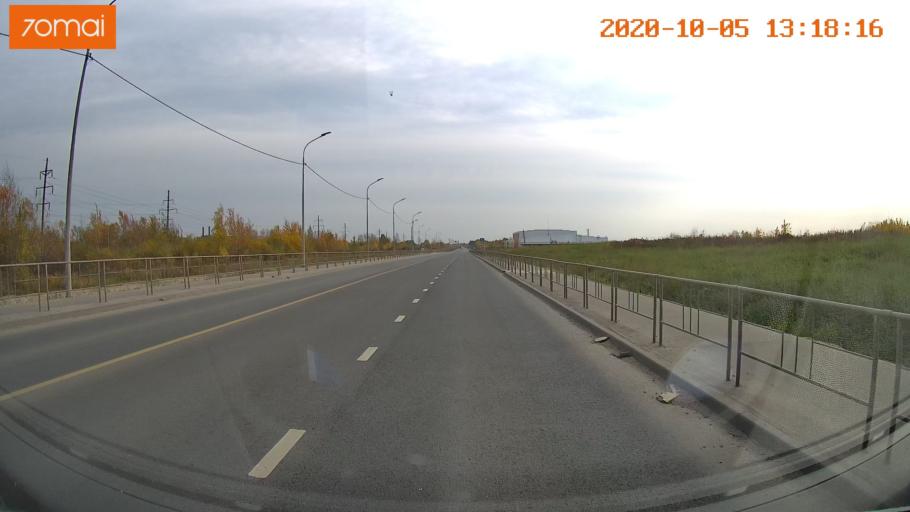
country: RU
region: Ivanovo
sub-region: Gorod Ivanovo
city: Ivanovo
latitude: 56.9787
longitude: 40.9184
